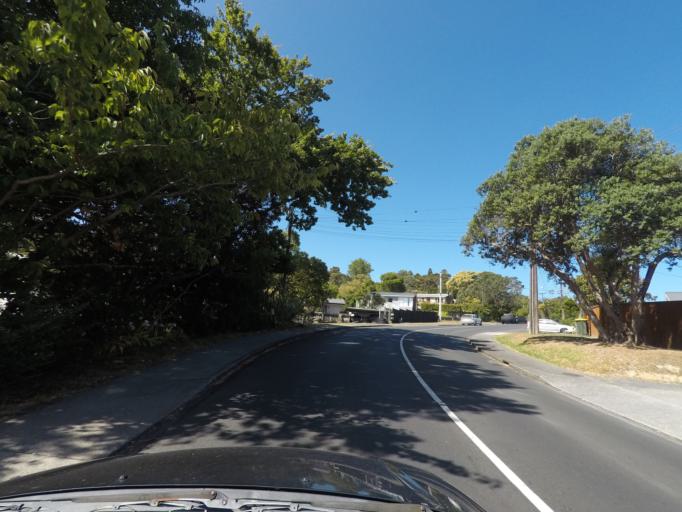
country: NZ
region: Auckland
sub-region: Auckland
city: Waitakere
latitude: -36.9224
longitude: 174.6579
